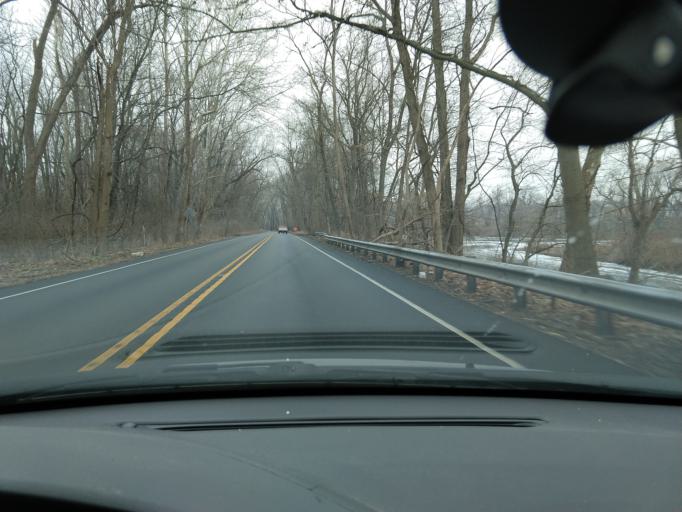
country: US
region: Pennsylvania
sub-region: Montgomery County
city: Stowe
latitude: 40.2382
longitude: -75.6936
